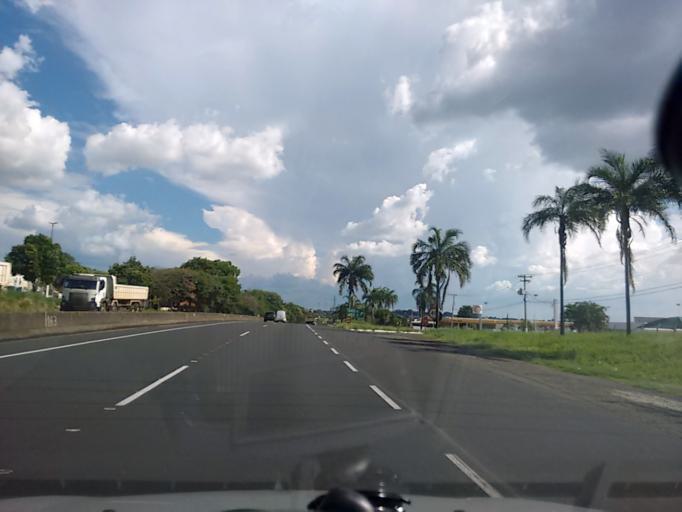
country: BR
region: Sao Paulo
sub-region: Marilia
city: Marilia
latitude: -22.2084
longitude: -49.9632
